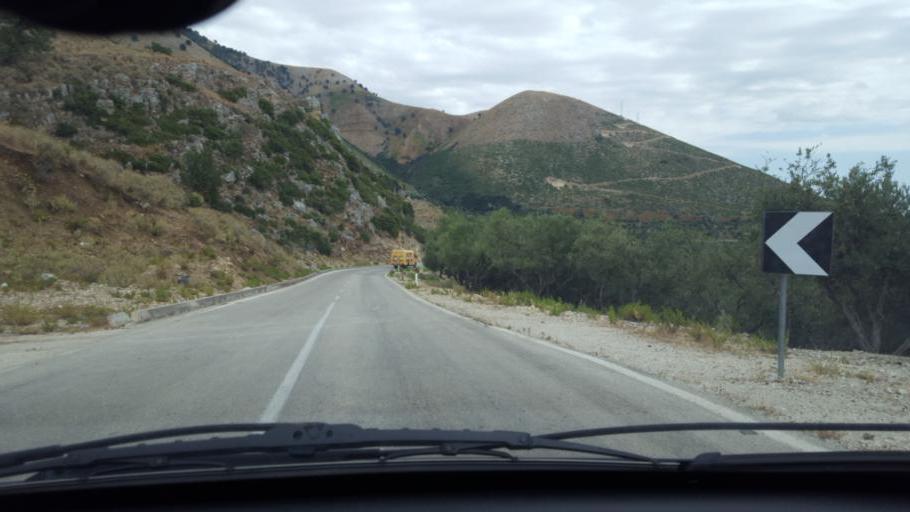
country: AL
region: Vlore
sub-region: Rrethi i Sarandes
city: Lukove
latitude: 40.0374
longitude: 19.8795
